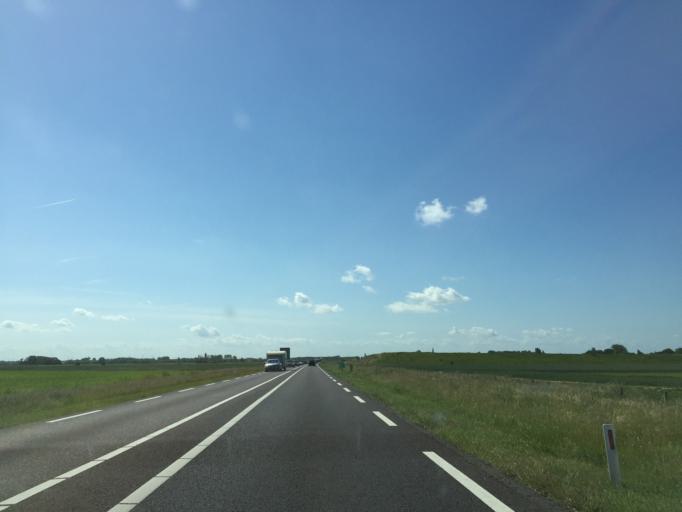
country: NL
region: Zeeland
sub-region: Gemeente Middelburg
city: Middelburg
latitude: 51.5371
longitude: 3.6087
